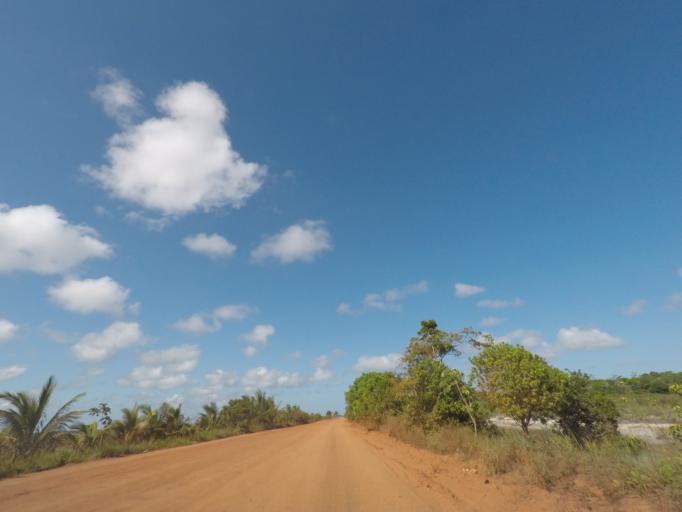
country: BR
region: Bahia
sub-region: Marau
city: Marau
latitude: -14.1765
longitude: -39.0208
